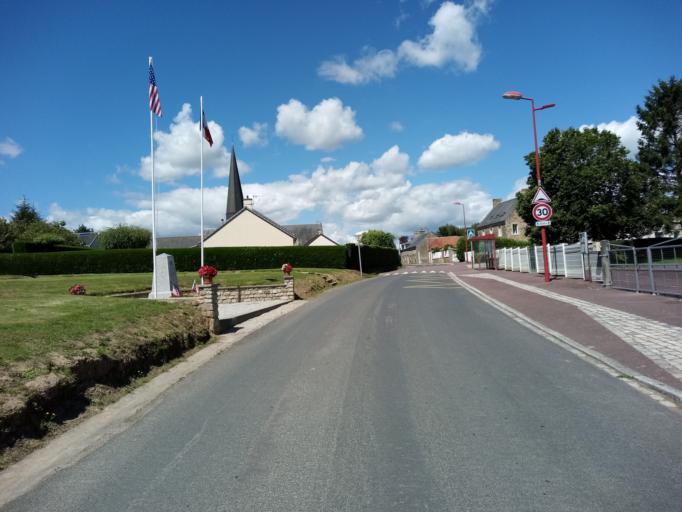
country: FR
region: Lower Normandy
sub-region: Departement de la Manche
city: Periers
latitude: 49.2801
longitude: -1.4234
